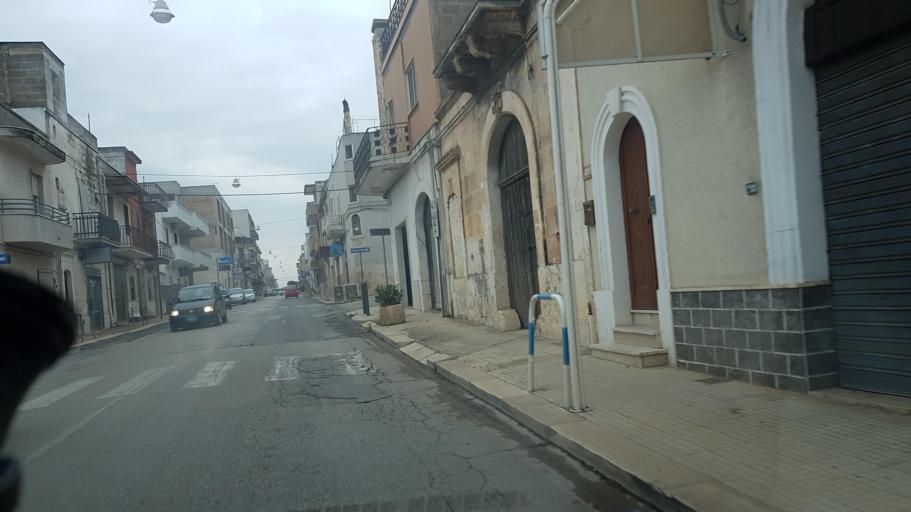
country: IT
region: Apulia
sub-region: Provincia di Brindisi
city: Carovigno
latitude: 40.7030
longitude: 17.6587
